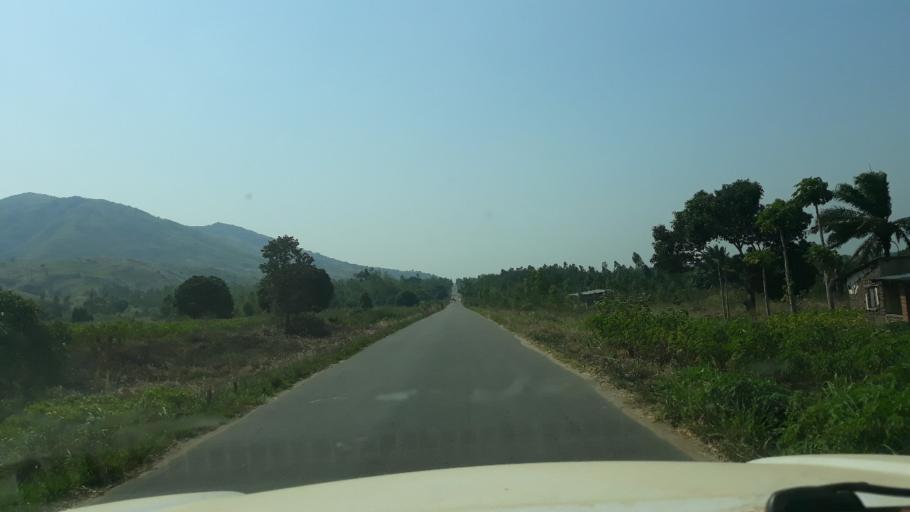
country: CD
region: South Kivu
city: Uvira
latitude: -3.3103
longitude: 29.1598
